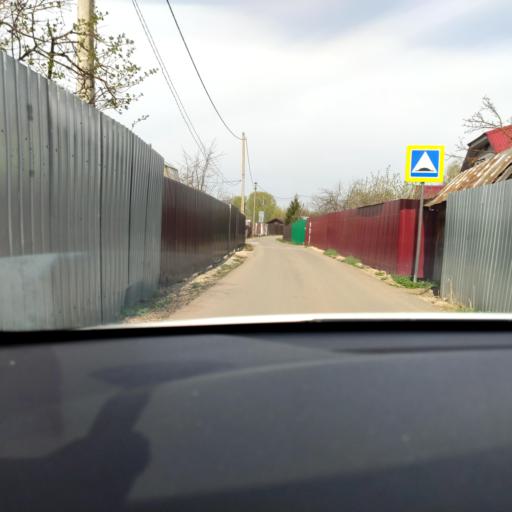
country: RU
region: Tatarstan
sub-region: Gorod Kazan'
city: Kazan
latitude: 55.8533
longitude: 49.1668
